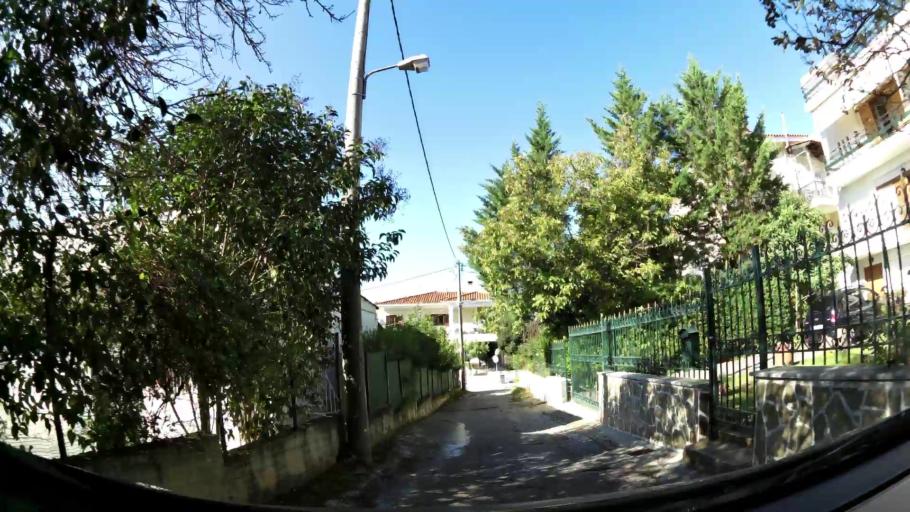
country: GR
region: Attica
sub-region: Nomarchia Anatolikis Attikis
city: Anoixi
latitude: 38.1322
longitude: 23.8637
